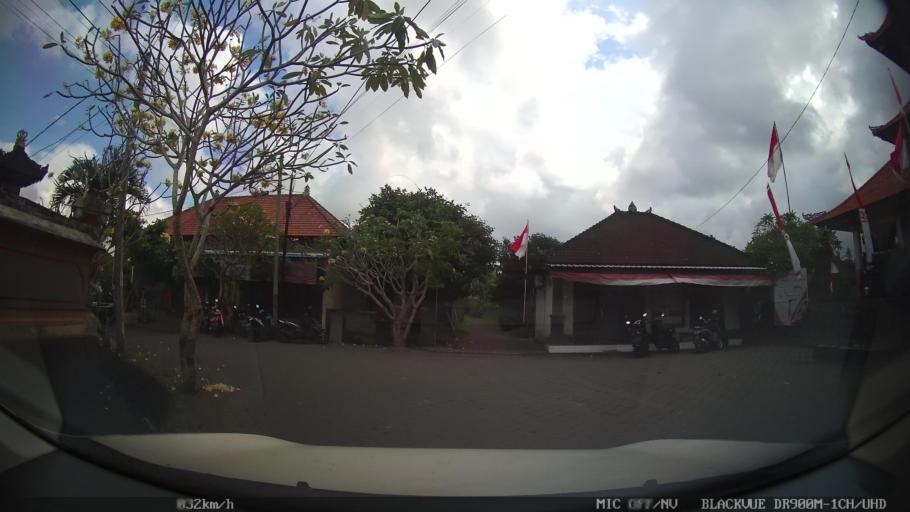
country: ID
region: Bali
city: Banjar Bucu
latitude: -8.5908
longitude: 115.2094
